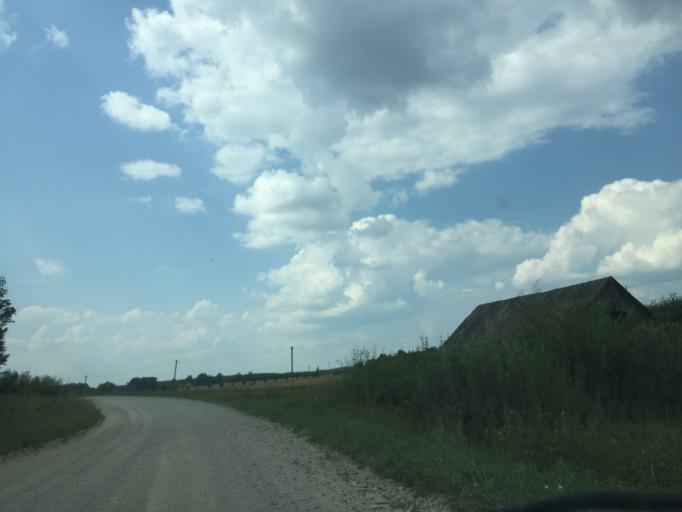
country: LV
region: Auces Novads
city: Auce
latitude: 56.4050
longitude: 23.0460
